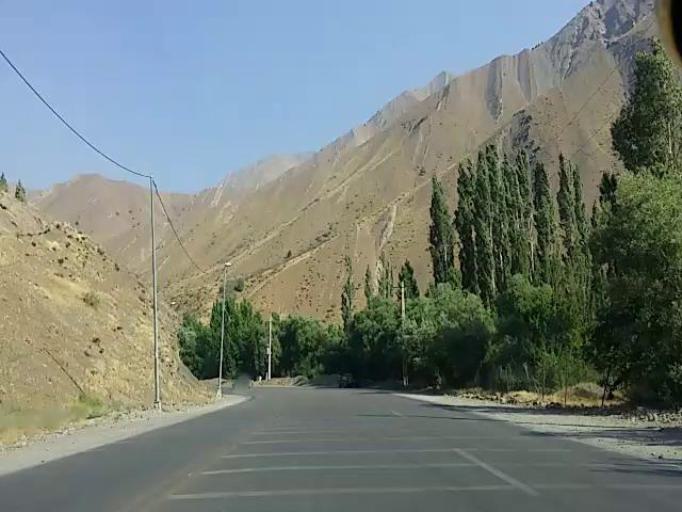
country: IR
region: Alborz
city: Karaj
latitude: 36.0333
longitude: 51.2047
